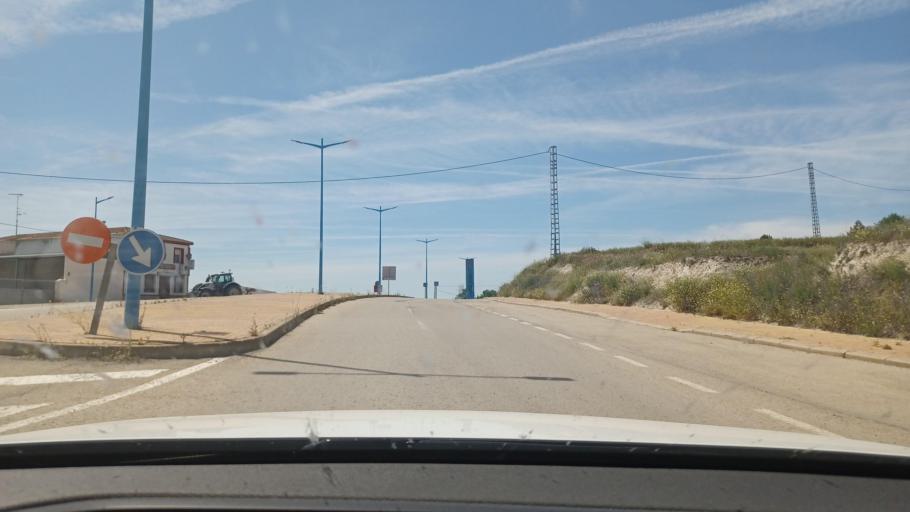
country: ES
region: Castille-La Mancha
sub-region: Provincia de Cuenca
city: Montalbo
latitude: 39.8812
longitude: -2.6734
